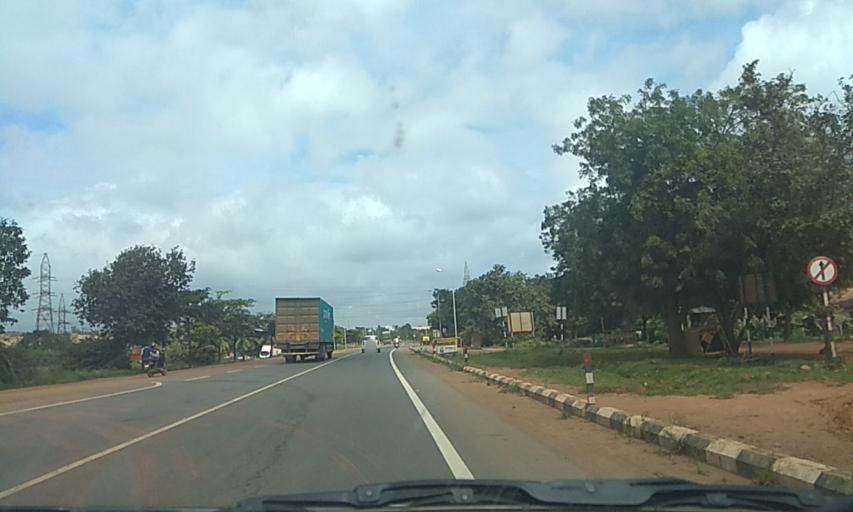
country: IN
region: Karnataka
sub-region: Dharwad
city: Hubli
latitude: 15.3275
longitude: 75.1214
